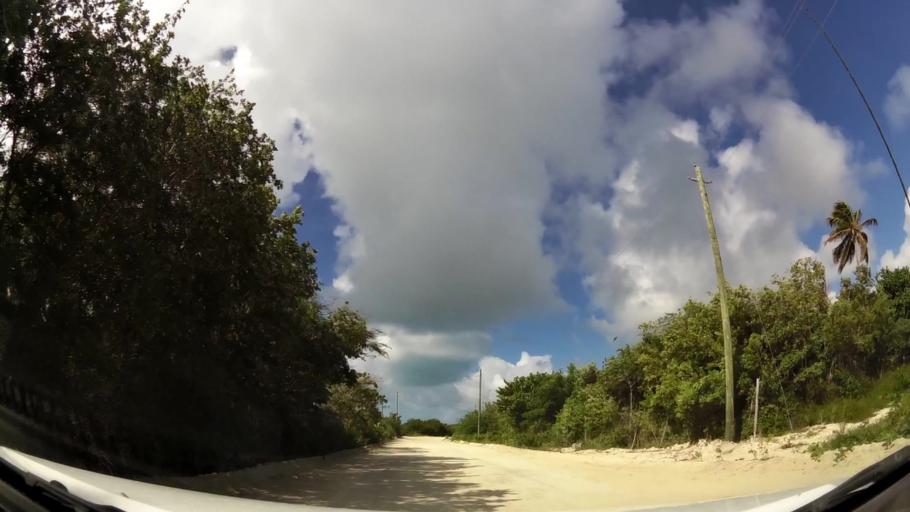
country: AG
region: Barbuda
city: Codrington
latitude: 17.5923
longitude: -61.8211
